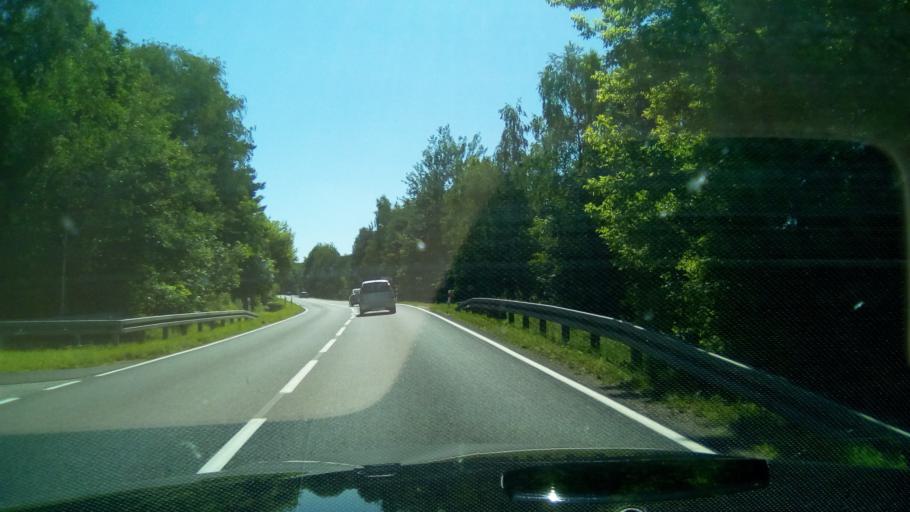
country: PL
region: Lodz Voivodeship
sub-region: Powiat tomaszowski
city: Inowlodz
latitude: 51.5265
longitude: 20.1872
